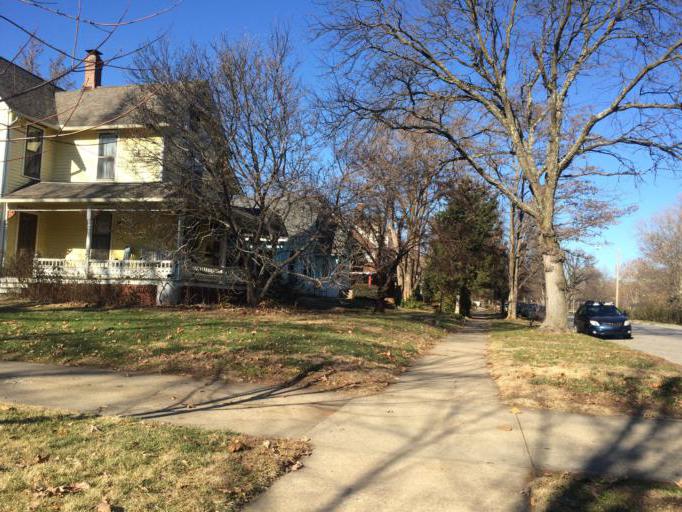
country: US
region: Kansas
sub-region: Douglas County
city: Lawrence
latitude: 38.9698
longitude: -95.2395
